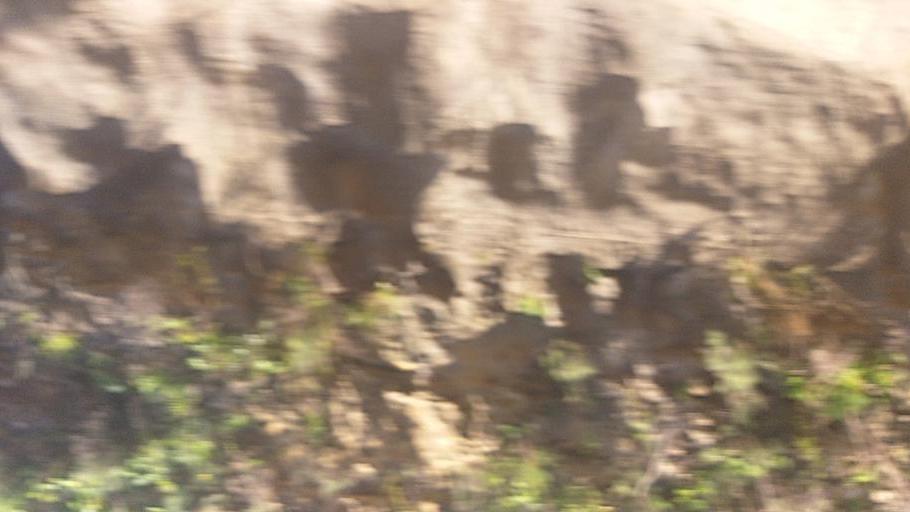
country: PT
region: Lisbon
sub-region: Lisbon
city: Lisbon
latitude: 38.7369
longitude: -9.1065
